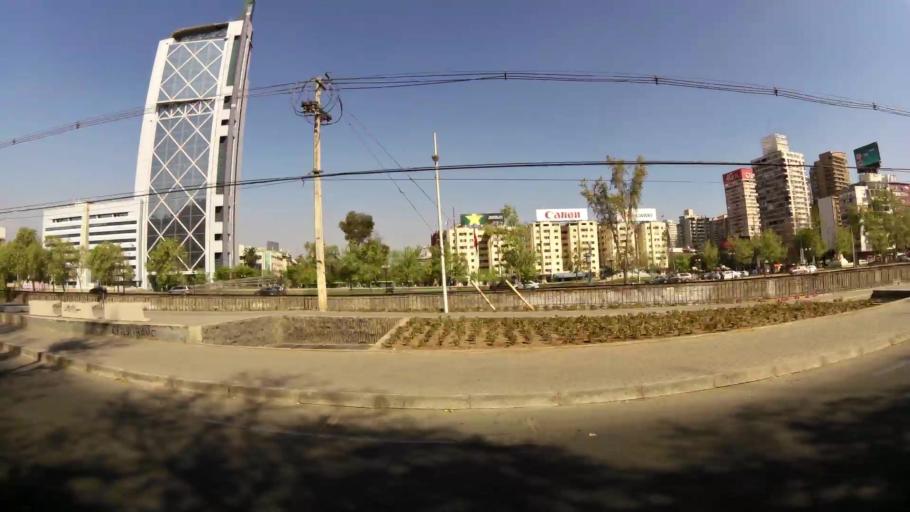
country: CL
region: Santiago Metropolitan
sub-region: Provincia de Santiago
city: Santiago
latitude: -33.4358
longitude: -70.6341
